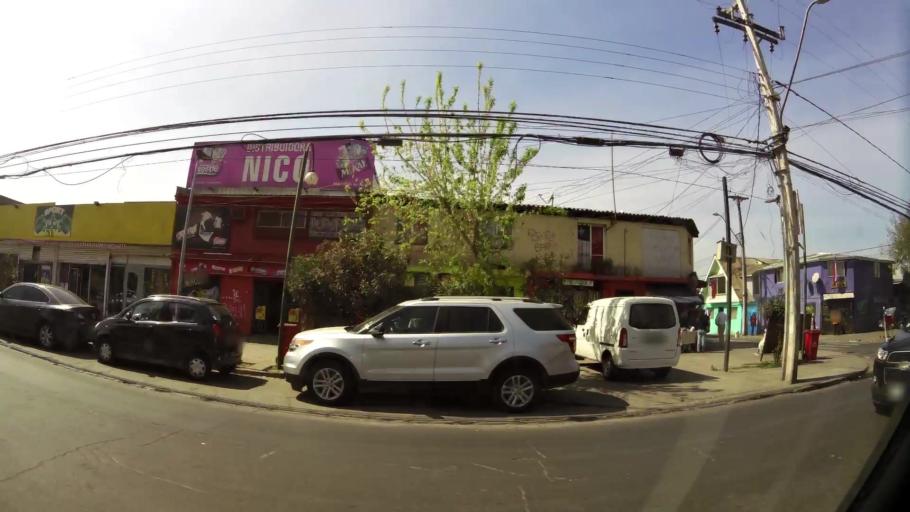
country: CL
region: Santiago Metropolitan
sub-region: Provincia de Santiago
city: Lo Prado
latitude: -33.4396
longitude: -70.7529
